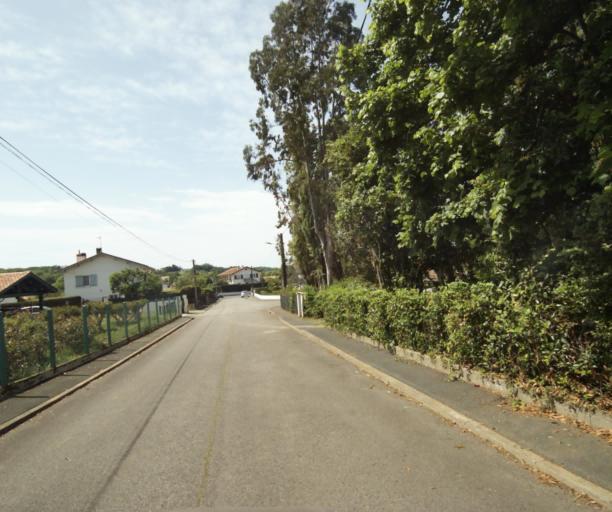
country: FR
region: Aquitaine
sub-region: Departement des Pyrenees-Atlantiques
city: Mouguerre
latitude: 43.4650
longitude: -1.4354
